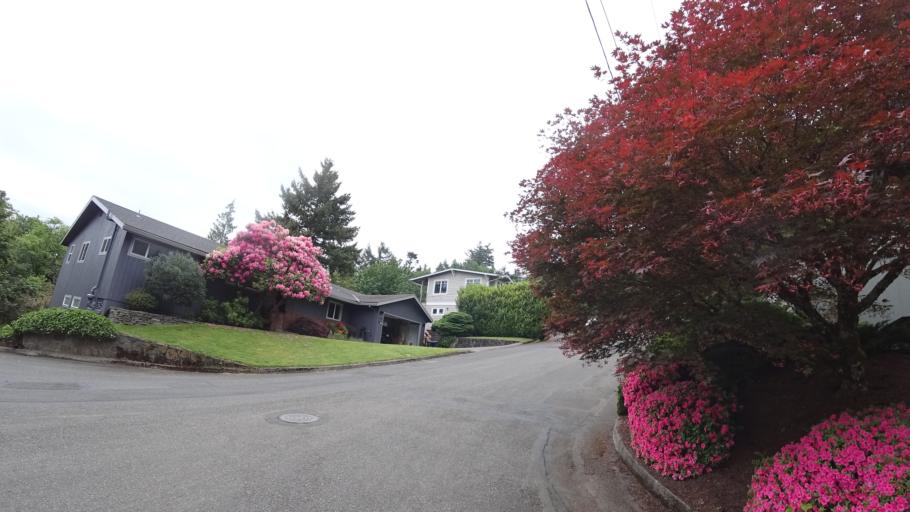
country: US
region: Oregon
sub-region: Multnomah County
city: Portland
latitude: 45.5000
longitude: -122.7012
